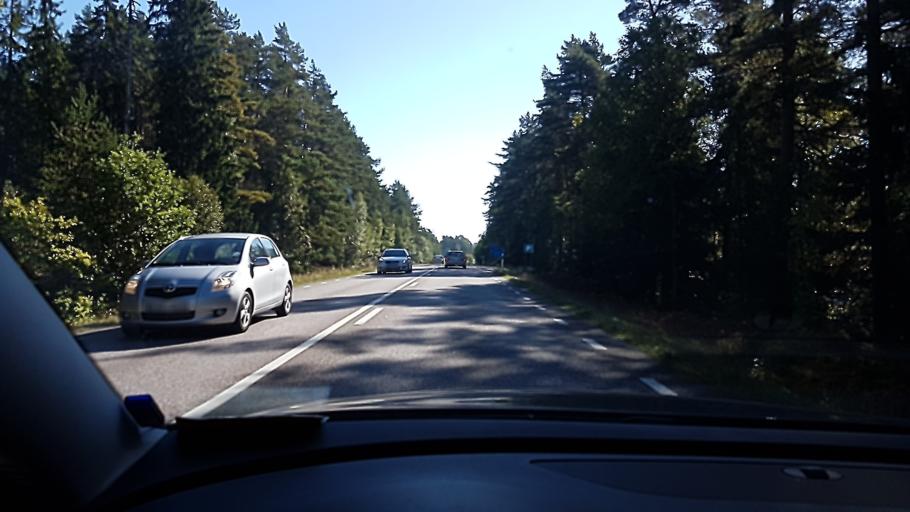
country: SE
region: Kronoberg
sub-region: Lessebo Kommun
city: Hovmantorp
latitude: 56.7883
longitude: 15.1452
